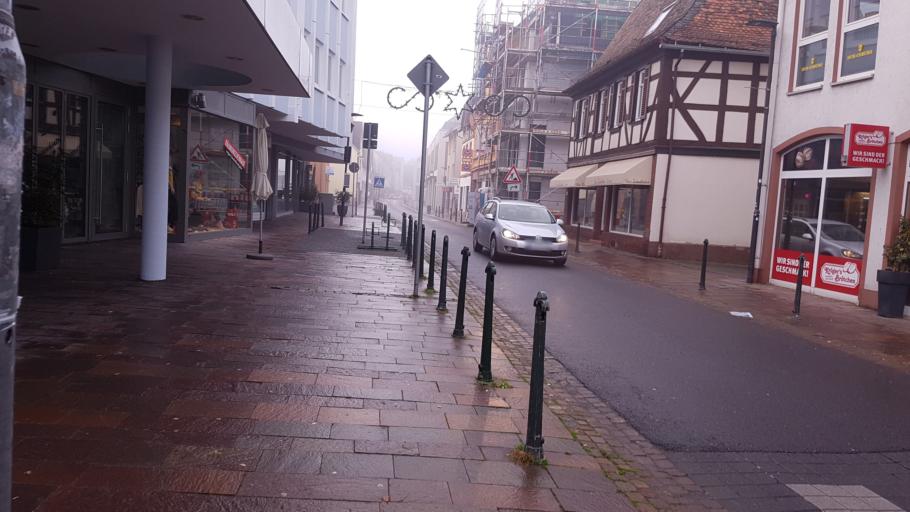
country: DE
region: Hesse
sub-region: Regierungsbezirk Darmstadt
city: Bad Vilbel
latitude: 50.1814
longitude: 8.7419
